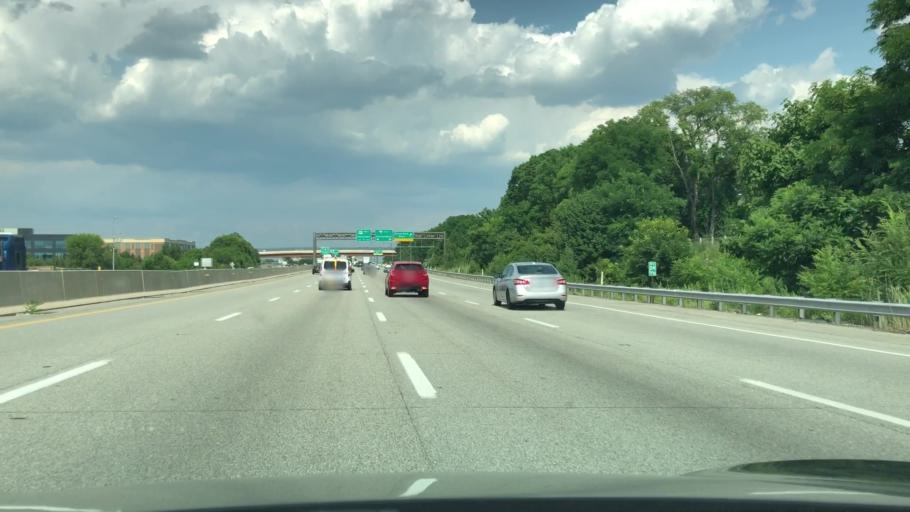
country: US
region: Pennsylvania
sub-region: Montgomery County
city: King of Prussia
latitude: 40.0760
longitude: -75.4164
